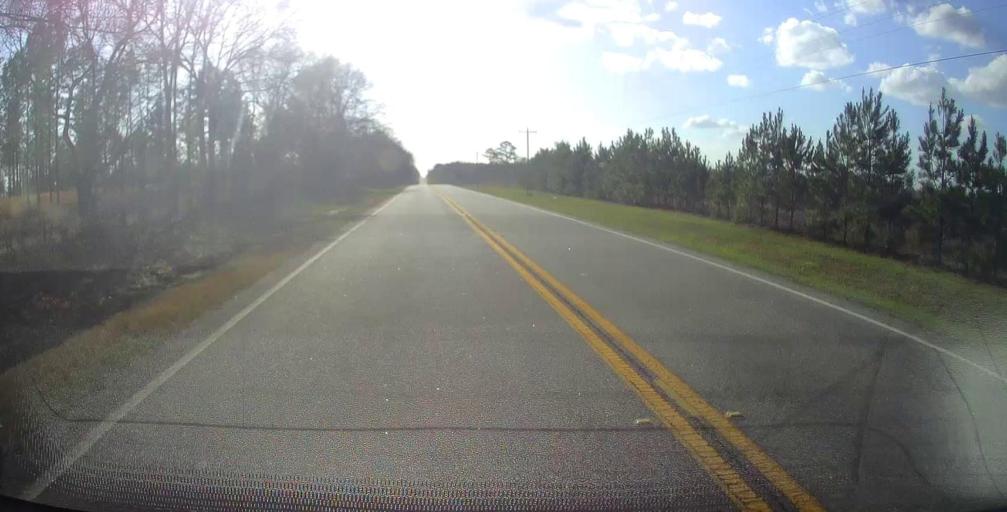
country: US
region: Georgia
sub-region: Wheeler County
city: Alamo
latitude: 32.1713
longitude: -82.6897
